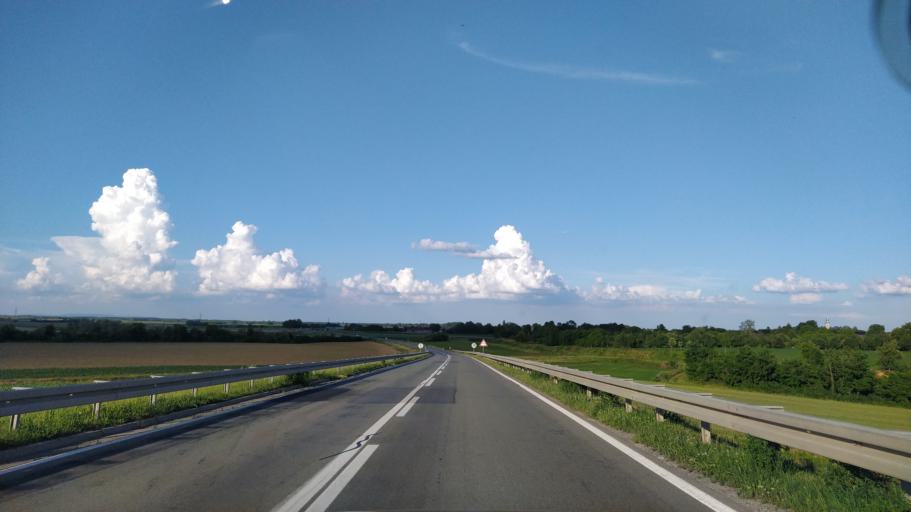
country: HR
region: Virovitick-Podravska
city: Slatina
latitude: 45.7260
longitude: 17.6442
